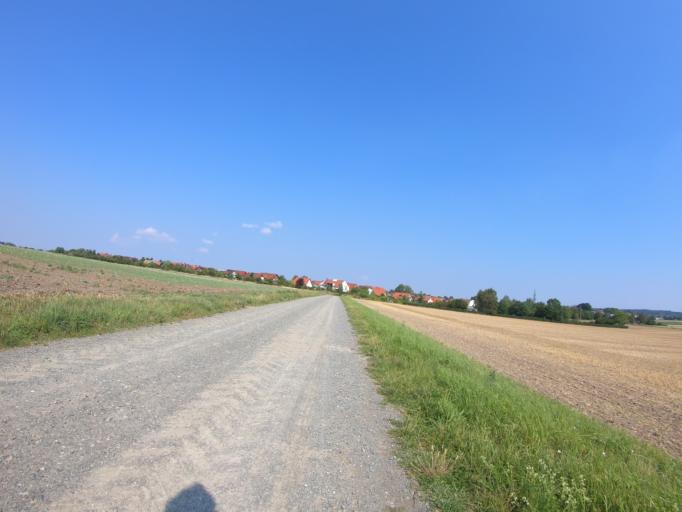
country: DE
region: Lower Saxony
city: Sickte
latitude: 52.2325
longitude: 10.5834
